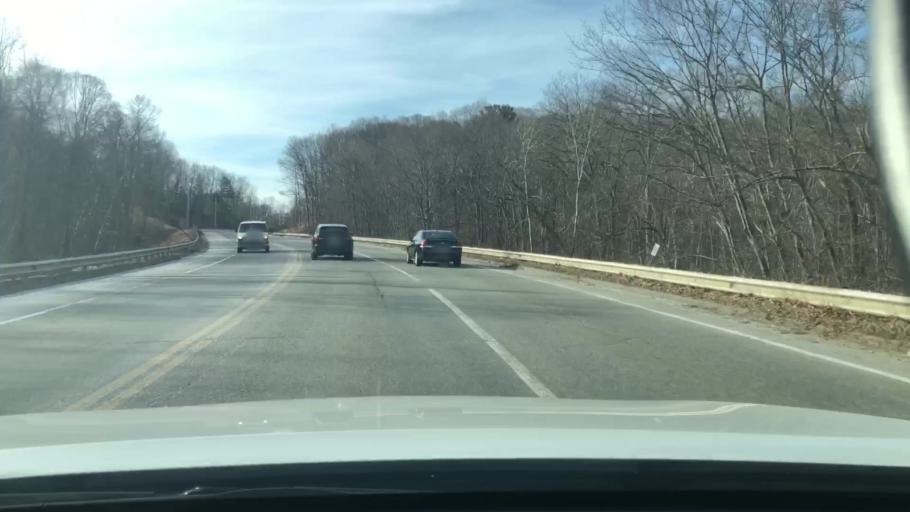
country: US
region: Massachusetts
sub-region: Worcester County
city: Grafton
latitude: 42.2053
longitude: -71.6672
